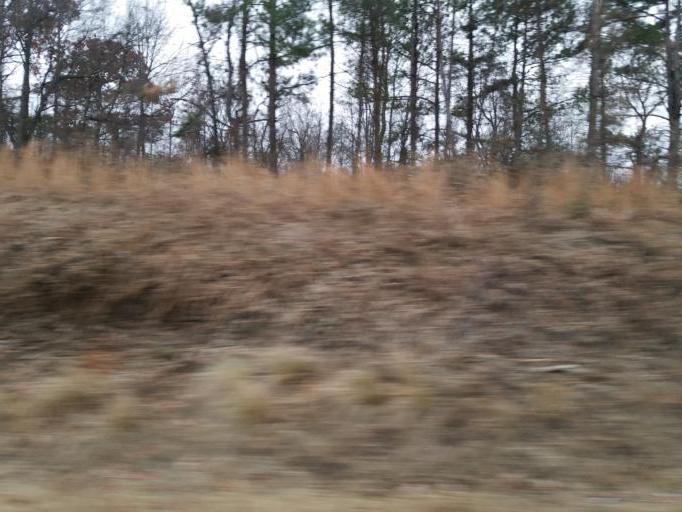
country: US
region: Georgia
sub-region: Dawson County
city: Dawsonville
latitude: 34.5024
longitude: -84.2054
